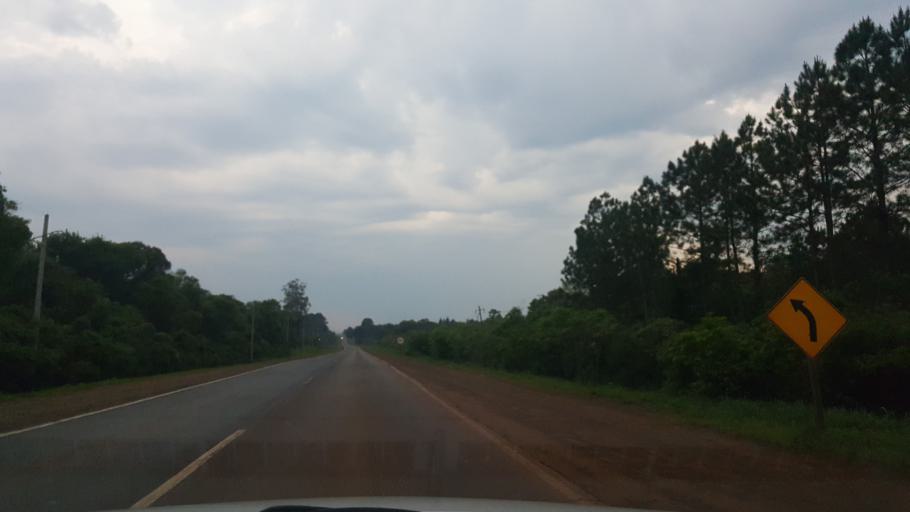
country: AR
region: Misiones
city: Jardin America
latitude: -27.0284
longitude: -55.2140
